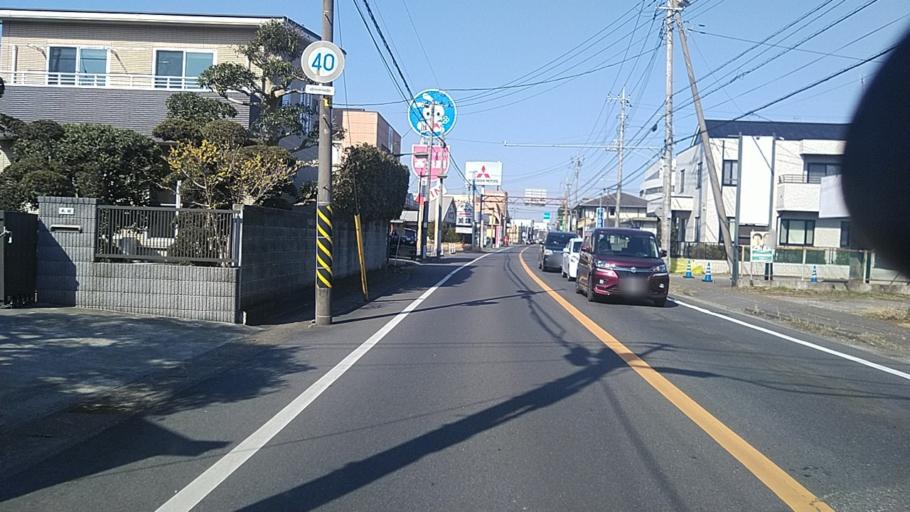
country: JP
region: Chiba
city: Mobara
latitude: 35.4331
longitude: 140.2935
